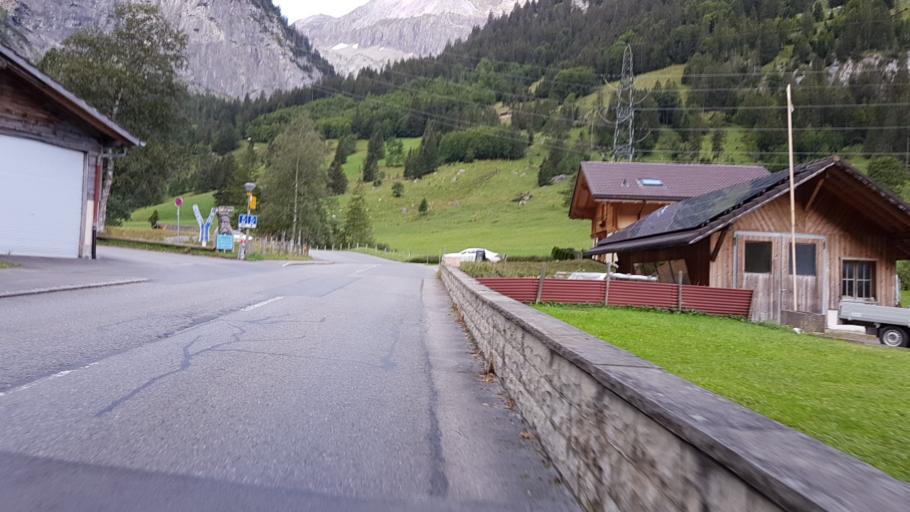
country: CH
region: Bern
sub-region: Frutigen-Niedersimmental District
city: Kandersteg
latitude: 46.4773
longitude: 7.6633
